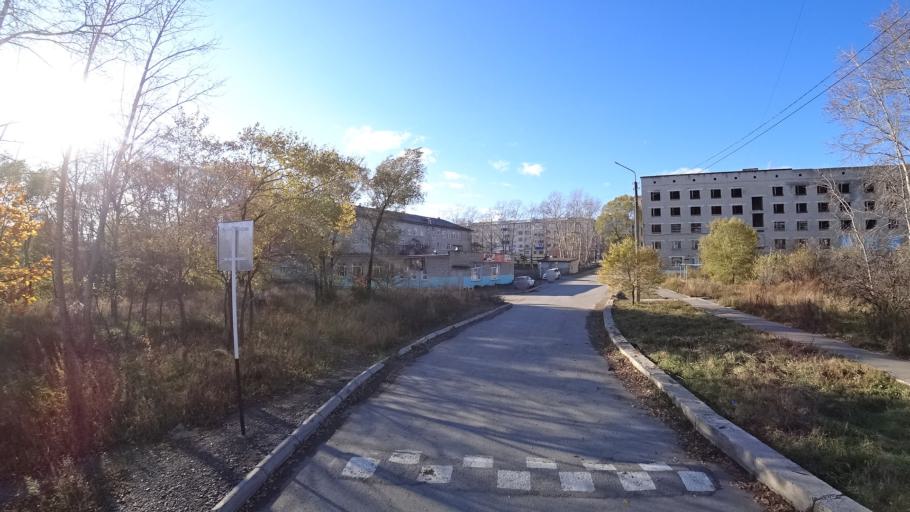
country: RU
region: Khabarovsk Krai
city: Amursk
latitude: 50.2321
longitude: 136.9091
